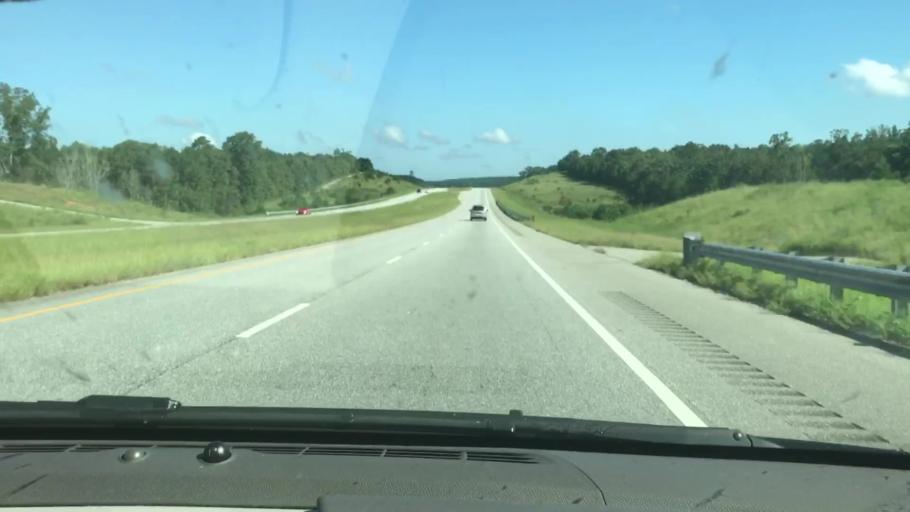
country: US
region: Alabama
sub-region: Barbour County
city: Eufaula
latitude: 32.1008
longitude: -85.1500
